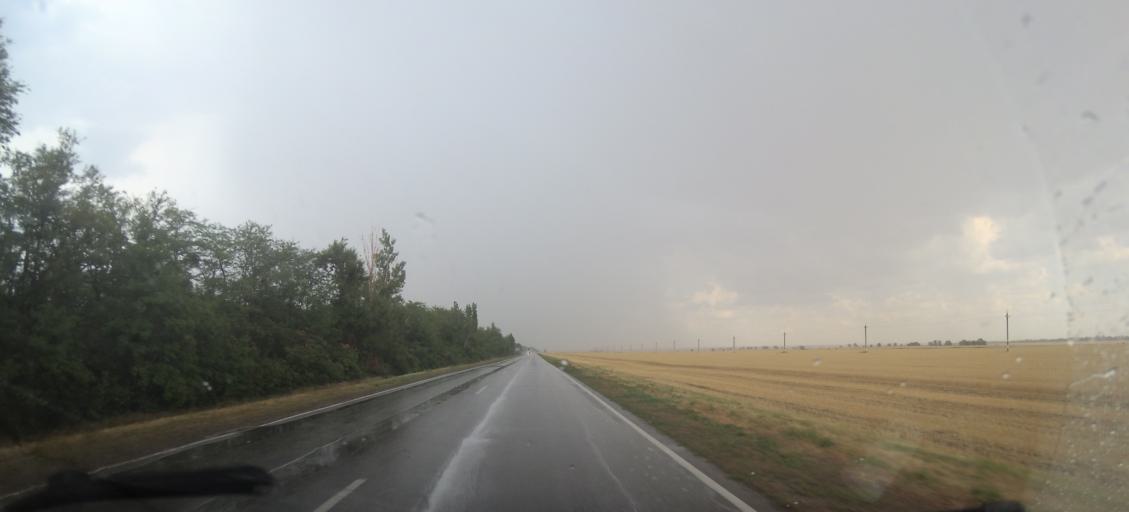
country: RU
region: Rostov
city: Proletarsk
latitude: 46.6629
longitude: 41.6870
